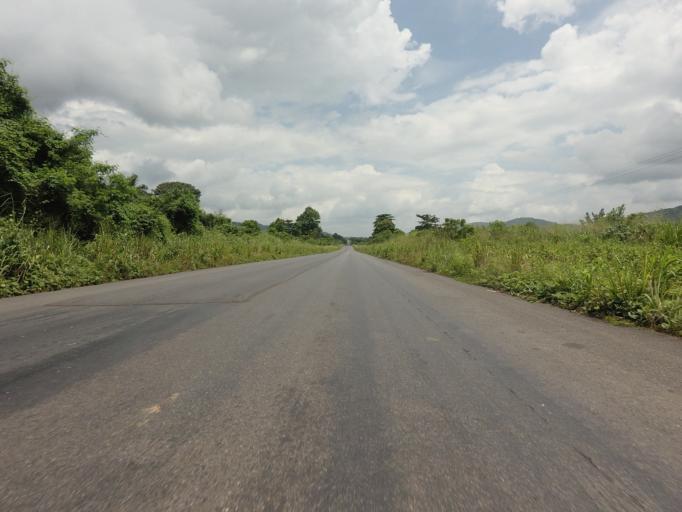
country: GH
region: Volta
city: Ho
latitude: 6.5658
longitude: 0.2685
